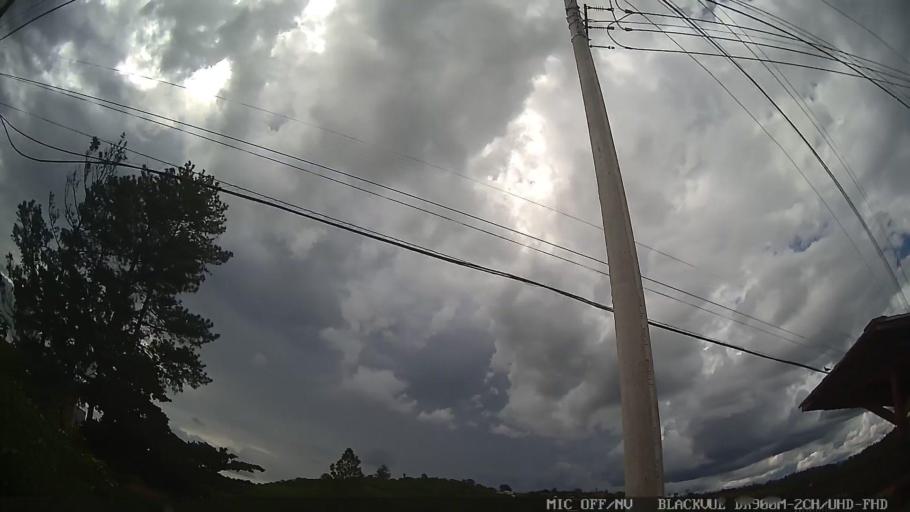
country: BR
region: Sao Paulo
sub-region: Pedreira
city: Pedreira
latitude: -22.7407
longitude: -46.9140
